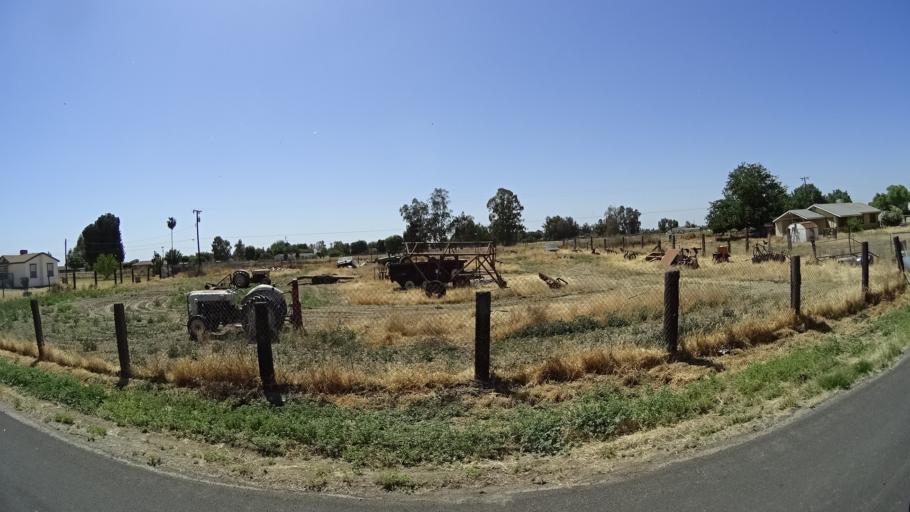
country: US
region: California
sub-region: Kings County
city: Lemoore
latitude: 36.2735
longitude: -119.7834
